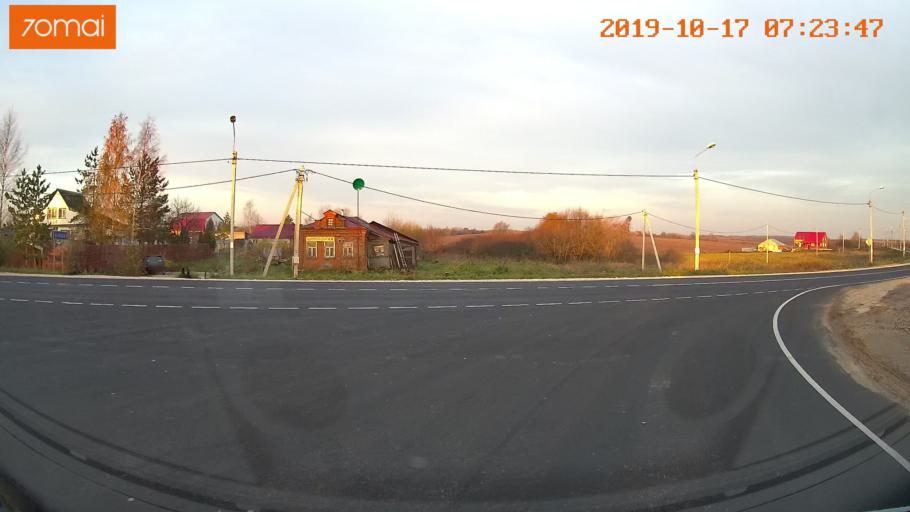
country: RU
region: Vladimir
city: Stavrovo
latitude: 56.3324
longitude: 40.1169
